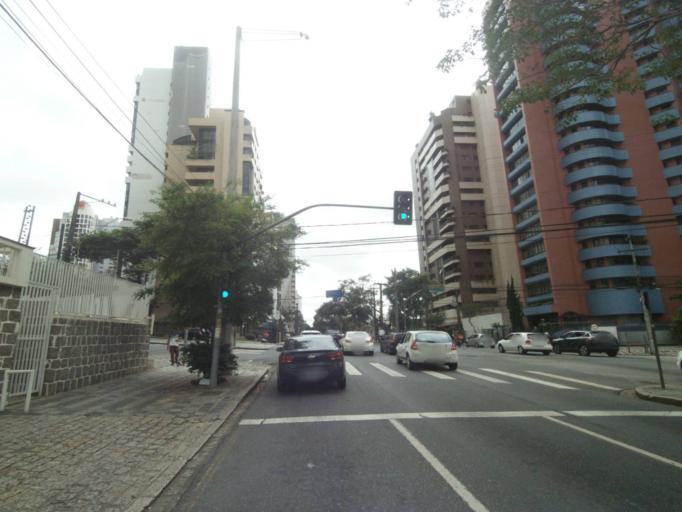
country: BR
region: Parana
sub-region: Curitiba
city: Curitiba
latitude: -25.4473
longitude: -49.2879
